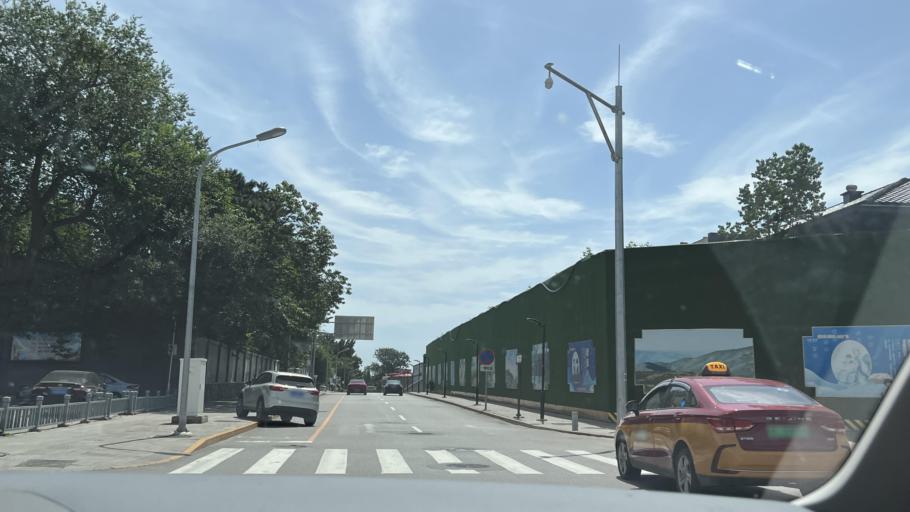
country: CN
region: Beijing
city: Xiangshan
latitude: 39.9921
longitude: 116.2000
